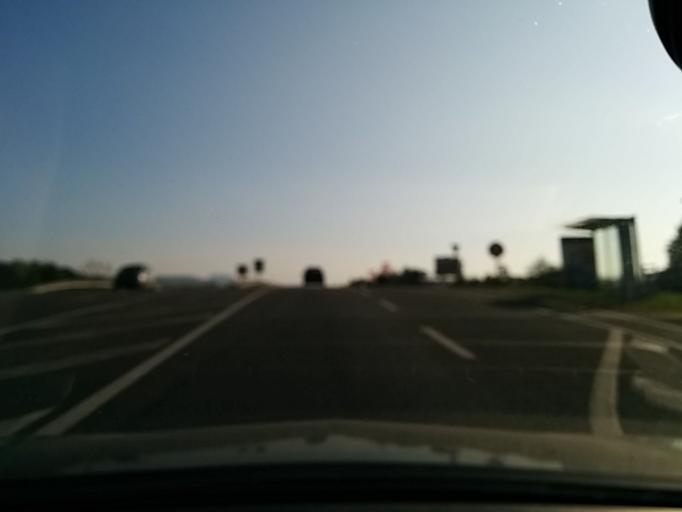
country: FR
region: Aquitaine
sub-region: Departement des Pyrenees-Atlantiques
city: Guethary
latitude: 43.4080
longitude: -1.6256
